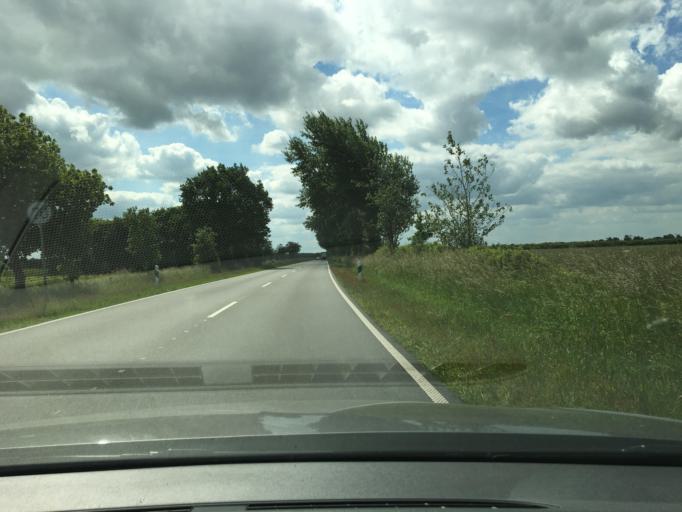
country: DE
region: Schleswig-Holstein
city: Klein Rheide
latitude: 54.4449
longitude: 9.4785
